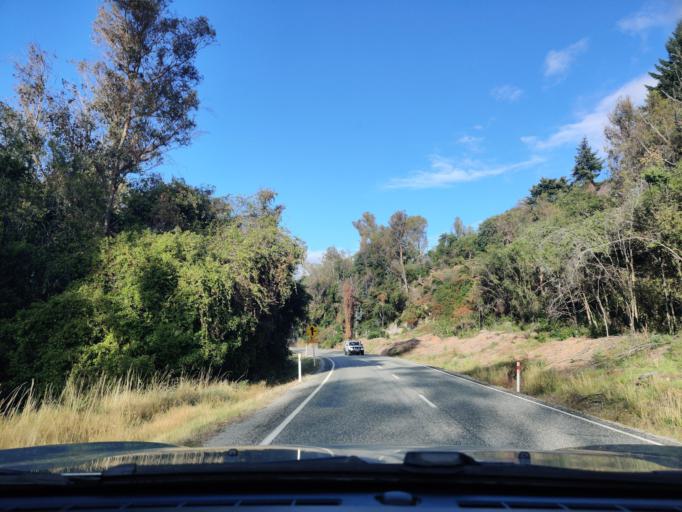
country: NZ
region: Otago
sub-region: Queenstown-Lakes District
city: Queenstown
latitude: -45.0450
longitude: 168.6320
